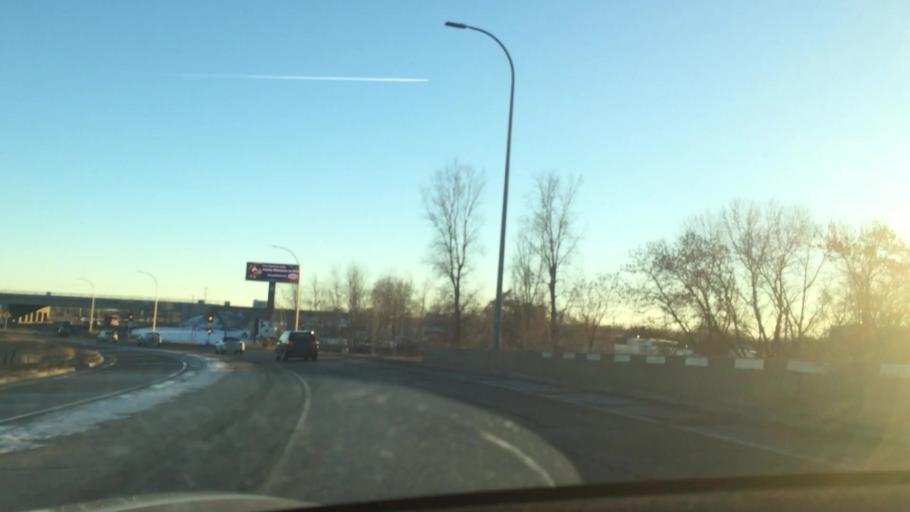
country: US
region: Minnesota
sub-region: Ramsey County
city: Mounds View
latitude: 45.1269
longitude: -93.1896
